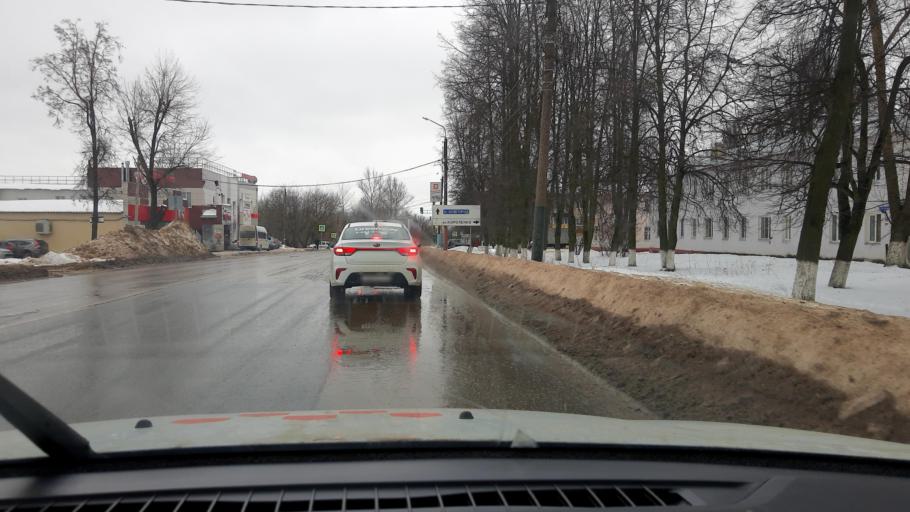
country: RU
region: Nizjnij Novgorod
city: Pavlovo
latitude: 55.9640
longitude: 43.1050
